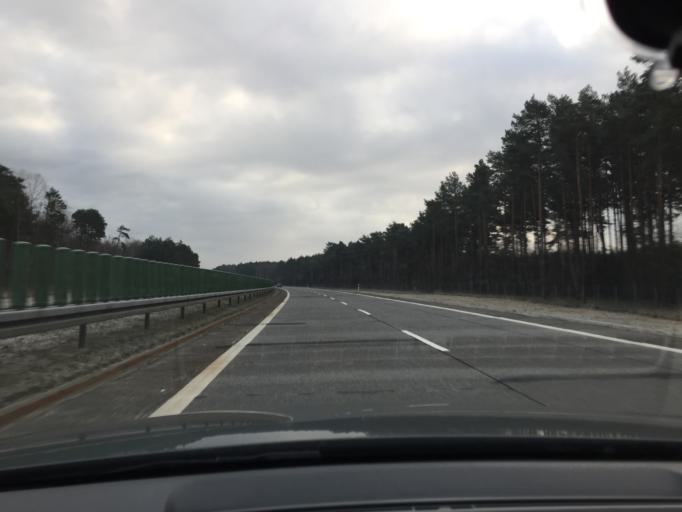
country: PL
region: Lubusz
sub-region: Powiat zarski
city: Trzebiel
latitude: 51.6263
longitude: 14.8844
